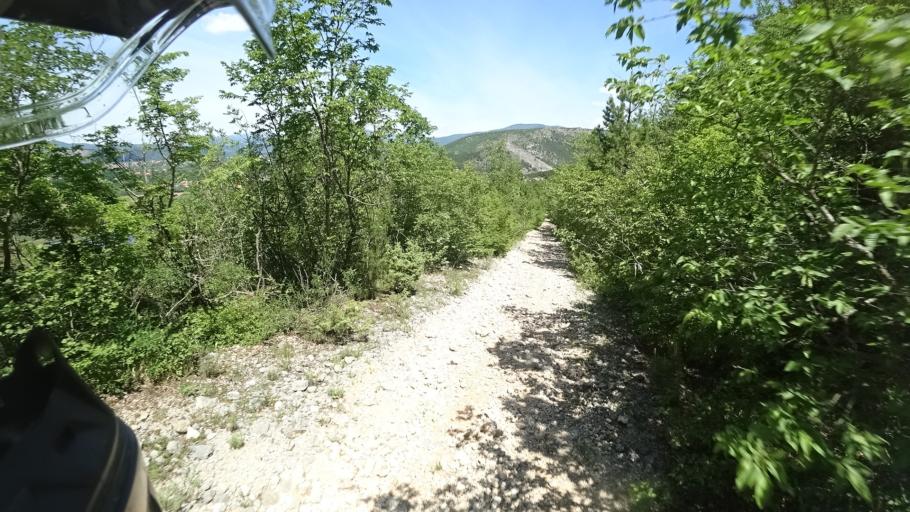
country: HR
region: Sibensko-Kniniska
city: Knin
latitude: 44.0338
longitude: 16.2289
